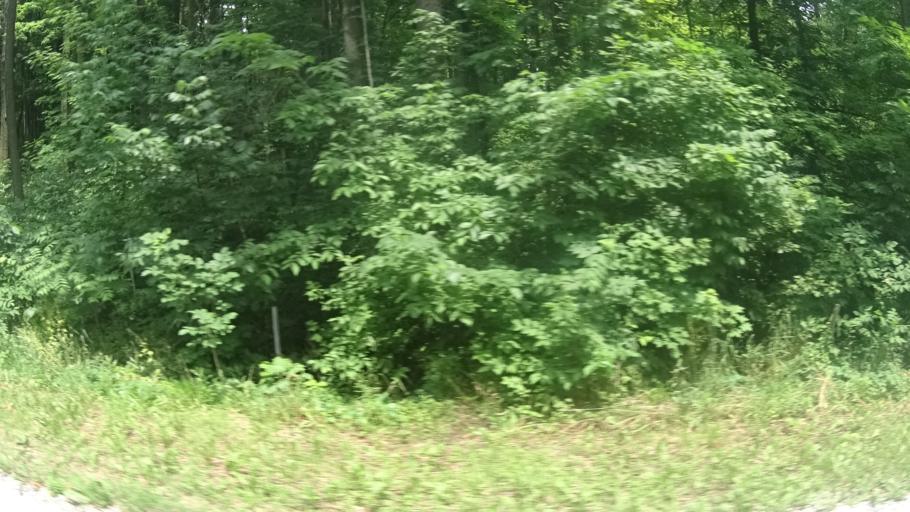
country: US
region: Ohio
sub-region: Erie County
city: Milan
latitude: 41.2886
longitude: -82.6441
